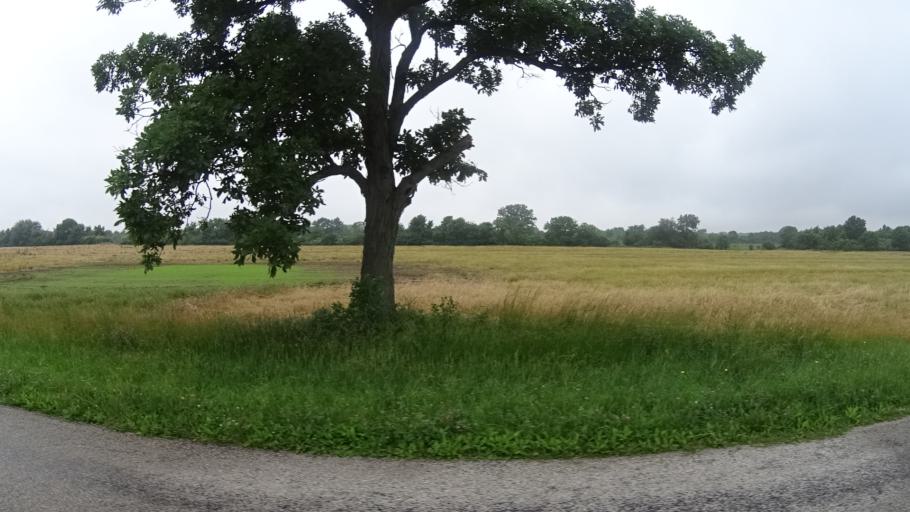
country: US
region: Ohio
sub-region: Huron County
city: Bellevue
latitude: 41.3600
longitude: -82.8172
